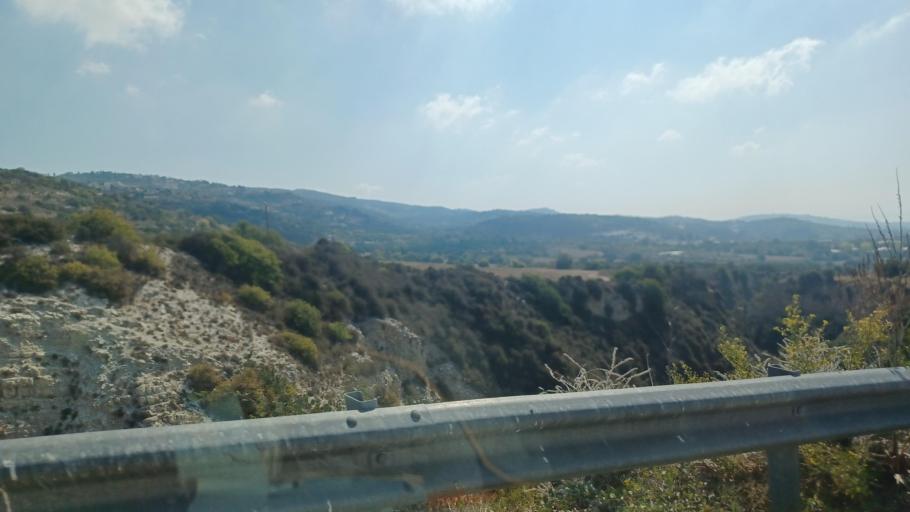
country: CY
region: Pafos
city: Mesogi
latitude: 34.8331
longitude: 32.4551
